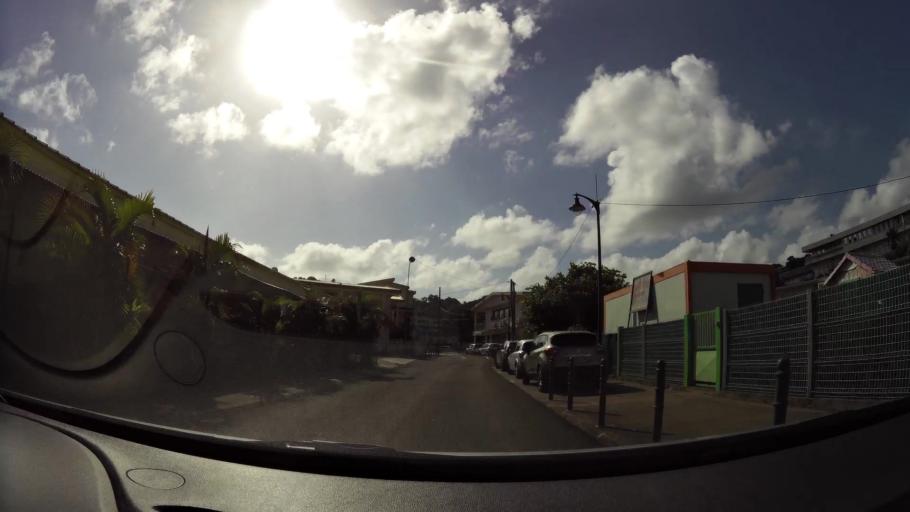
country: MQ
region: Martinique
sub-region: Martinique
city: La Trinite
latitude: 14.7373
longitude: -60.9634
